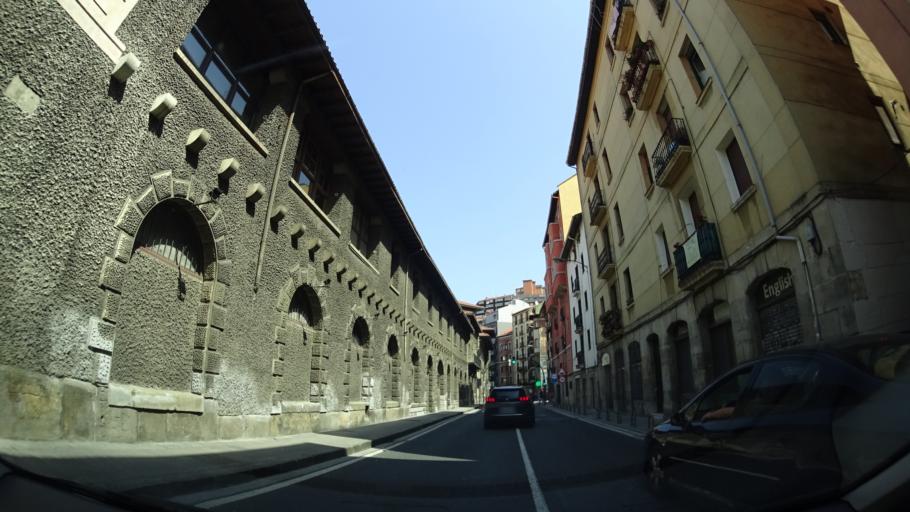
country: ES
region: Basque Country
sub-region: Bizkaia
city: Santutxu
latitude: 43.2532
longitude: -2.9215
